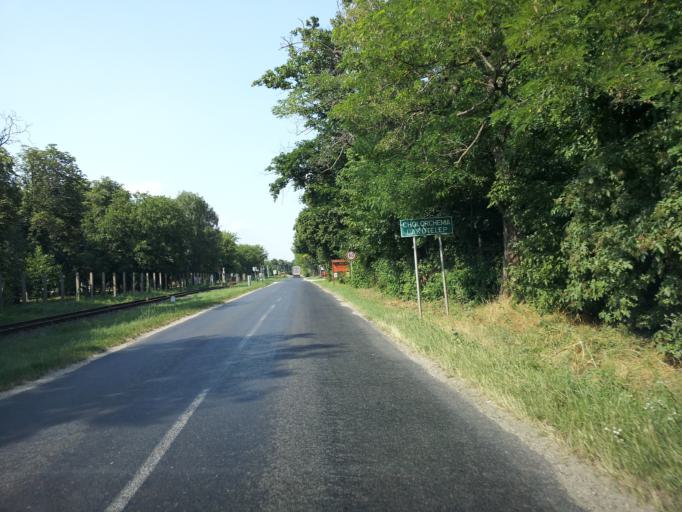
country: HU
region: Veszprem
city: Berhida
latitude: 47.1035
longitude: 18.0967
